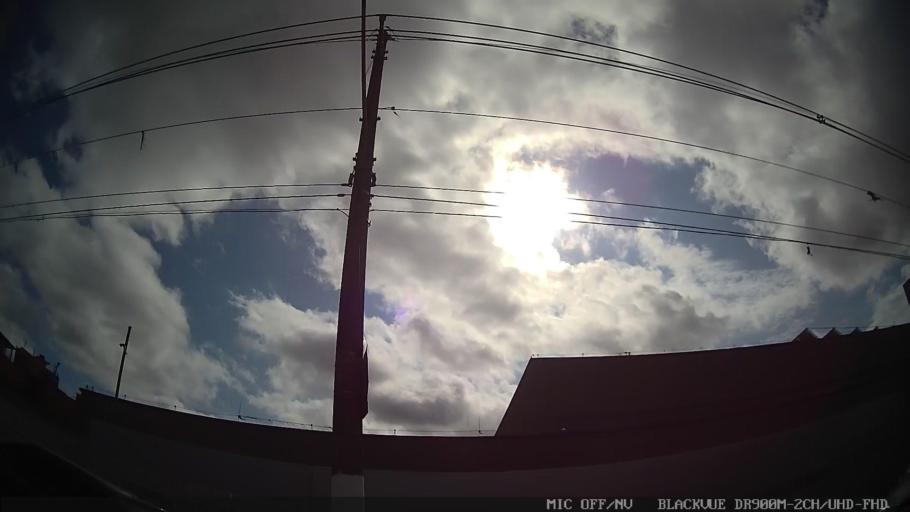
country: BR
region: Sao Paulo
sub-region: Guarulhos
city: Guarulhos
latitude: -23.5181
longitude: -46.4762
